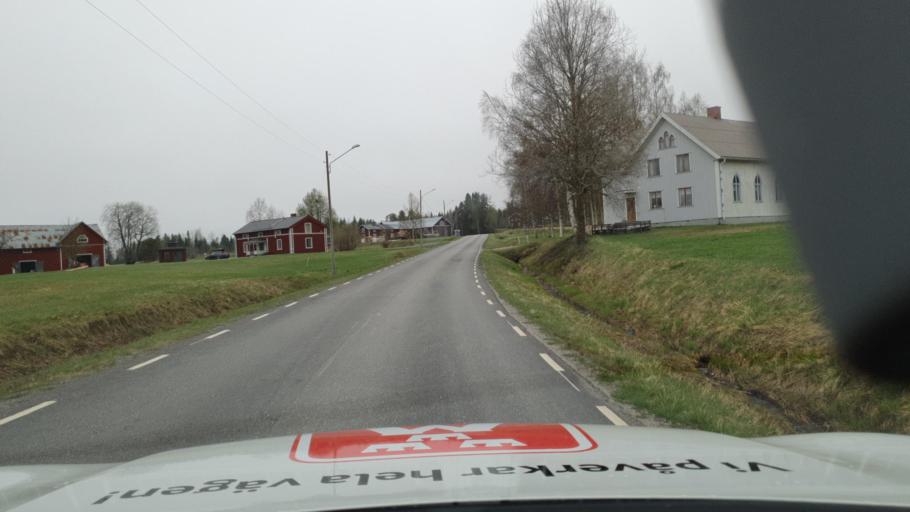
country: SE
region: Vaesterbotten
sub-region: Nordmalings Kommun
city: Nordmaling
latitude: 63.7071
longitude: 19.5891
